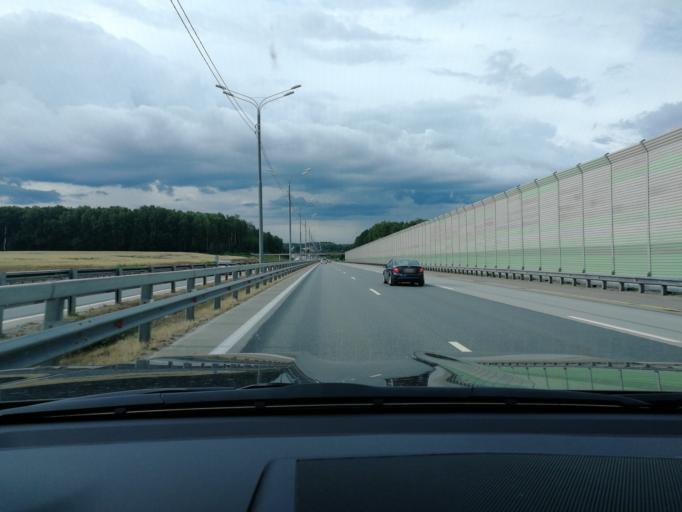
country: RU
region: Moskovskaya
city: Barybino
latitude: 55.2654
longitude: 37.8672
